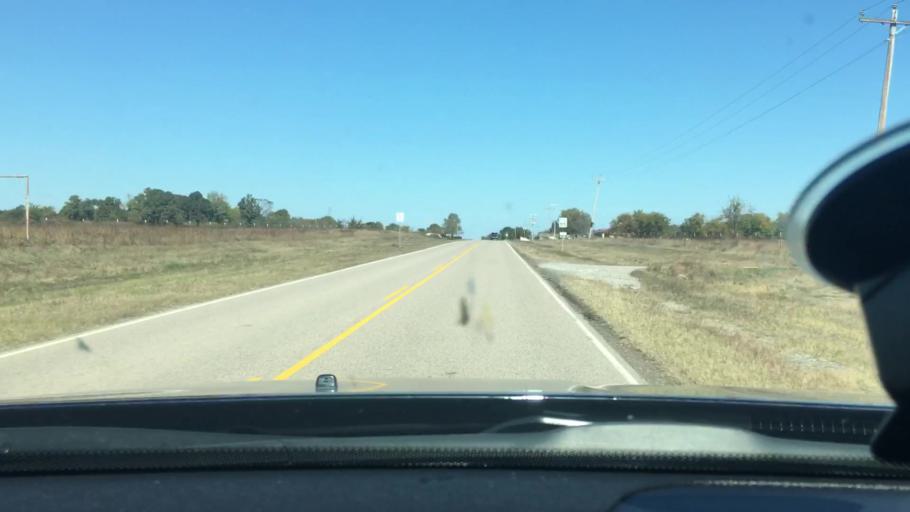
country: US
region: Oklahoma
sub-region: Johnston County
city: Tishomingo
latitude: 34.4385
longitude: -96.6359
